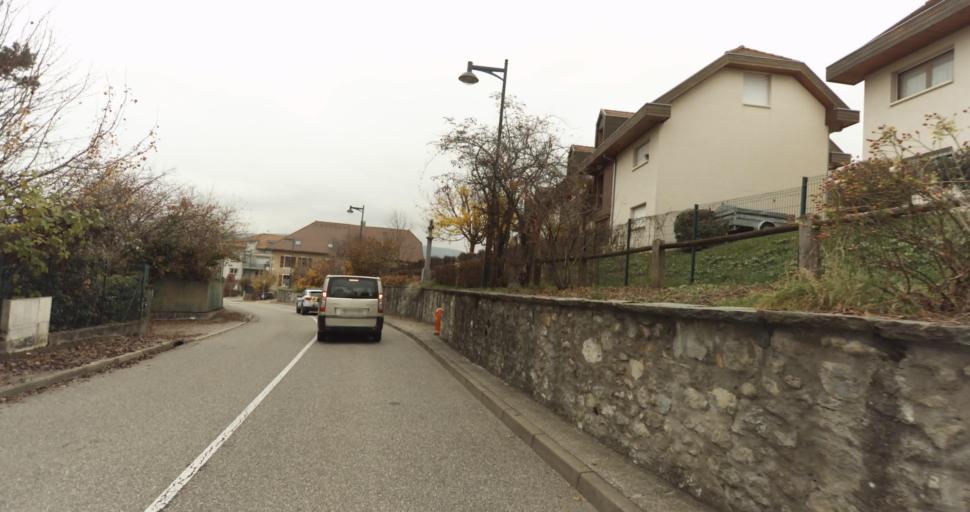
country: FR
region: Rhone-Alpes
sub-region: Departement de la Haute-Savoie
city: Annecy-le-Vieux
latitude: 45.9266
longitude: 6.1313
